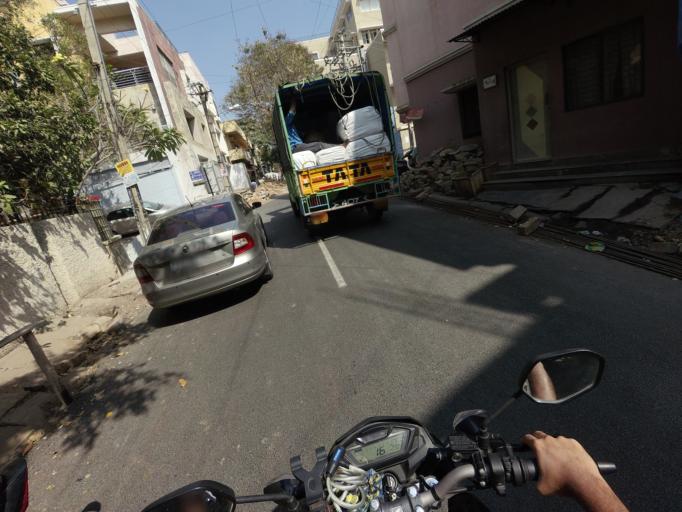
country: IN
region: Karnataka
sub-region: Bangalore Urban
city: Bangalore
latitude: 12.9646
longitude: 77.5428
